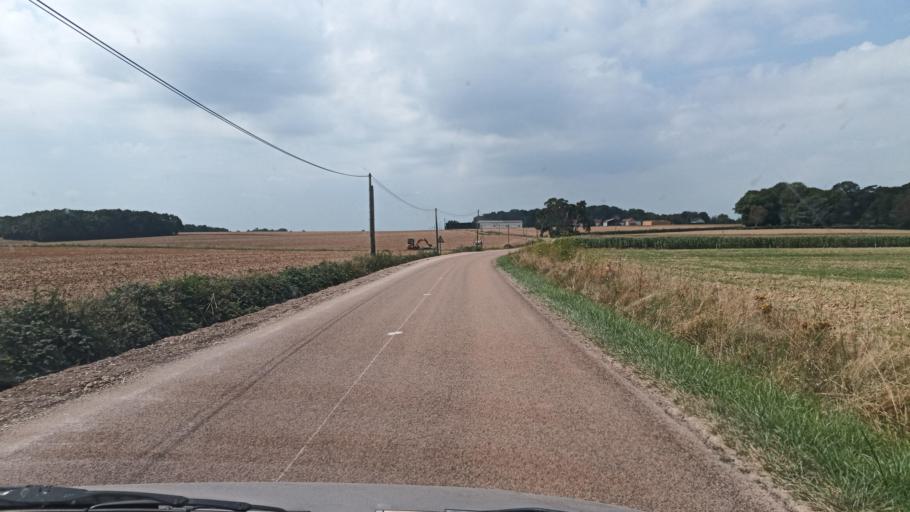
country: FR
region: Bourgogne
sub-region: Departement de l'Yonne
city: Saint-Julien-du-Sault
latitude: 48.0493
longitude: 3.2199
